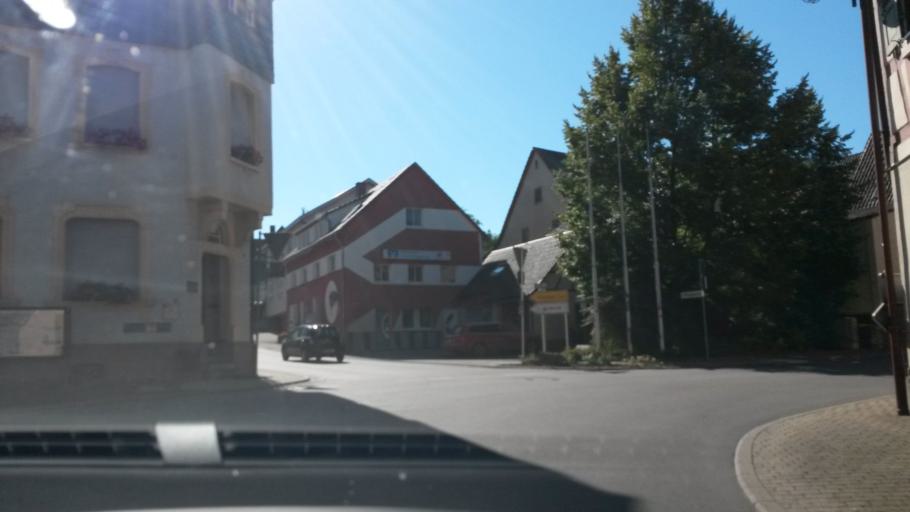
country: DE
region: Baden-Wuerttemberg
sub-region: Karlsruhe Region
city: Eisingen
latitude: 48.9477
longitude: 8.6685
